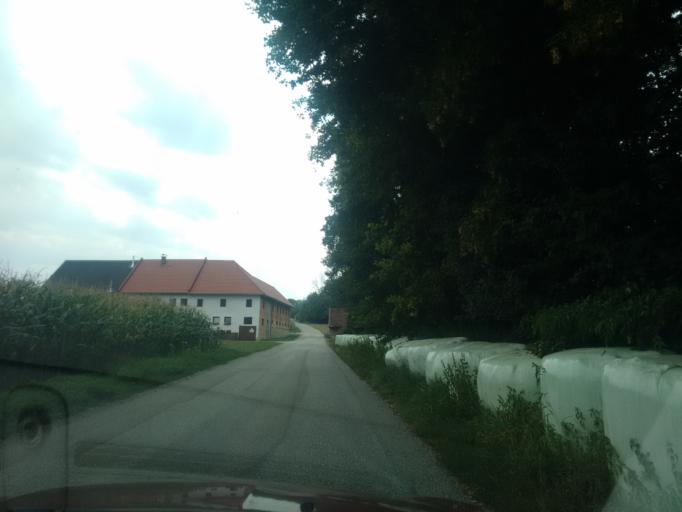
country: AT
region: Upper Austria
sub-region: Politischer Bezirk Grieskirchen
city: Bad Schallerbach
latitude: 48.2591
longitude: 13.9140
